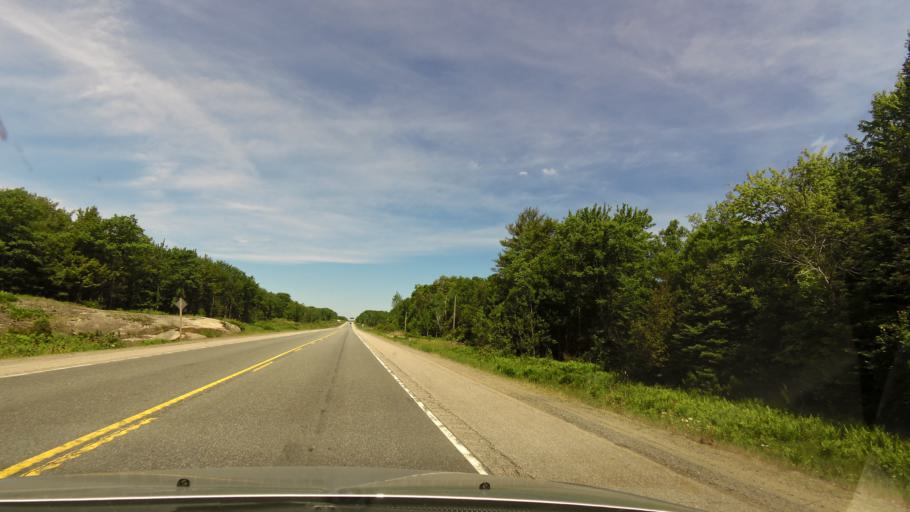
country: CA
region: Ontario
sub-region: Parry Sound District
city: Parry Sound
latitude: 45.4815
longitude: -80.1843
